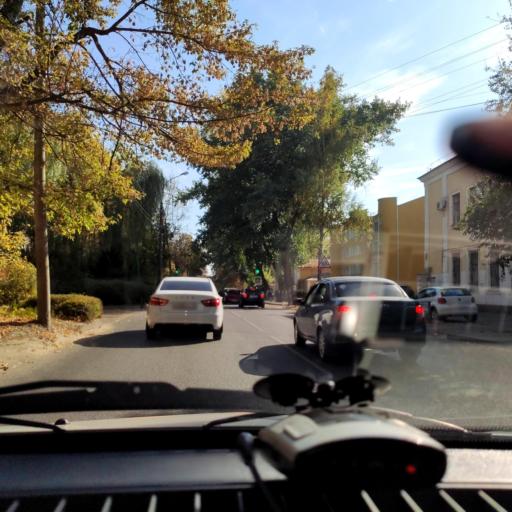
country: RU
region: Voronezj
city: Voronezh
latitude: 51.7167
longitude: 39.2218
